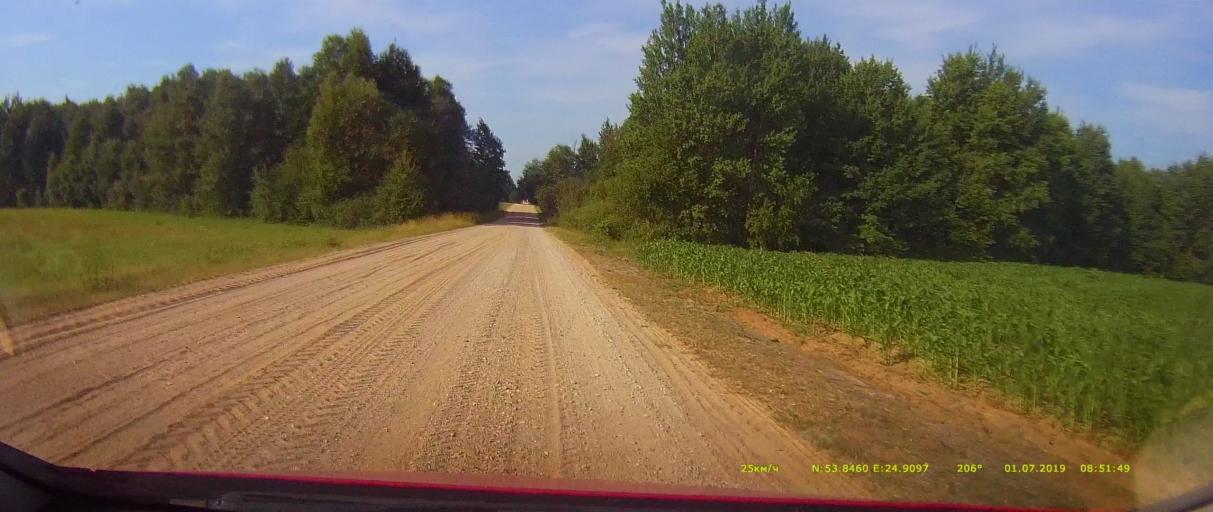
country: BY
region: Grodnenskaya
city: Shchuchin
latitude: 53.8461
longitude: 24.9097
